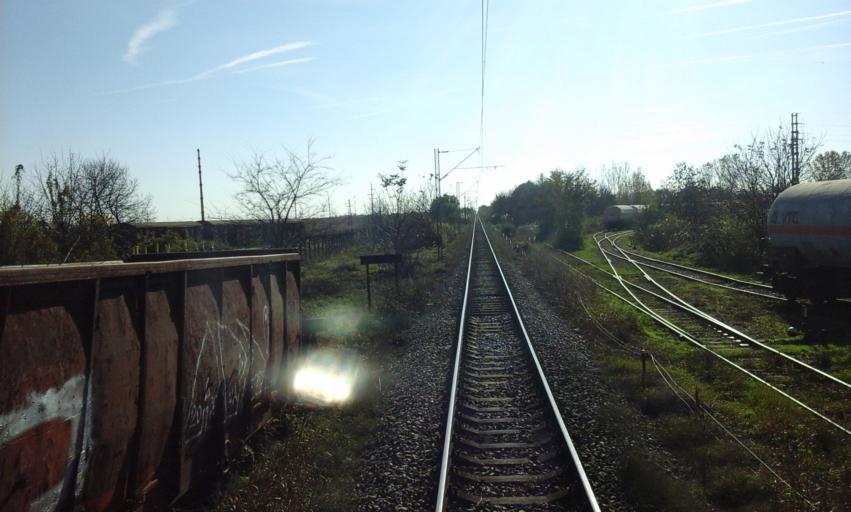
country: RS
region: Autonomna Pokrajina Vojvodina
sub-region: Severnobacki Okrug
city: Subotica
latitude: 46.0595
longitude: 19.6868
